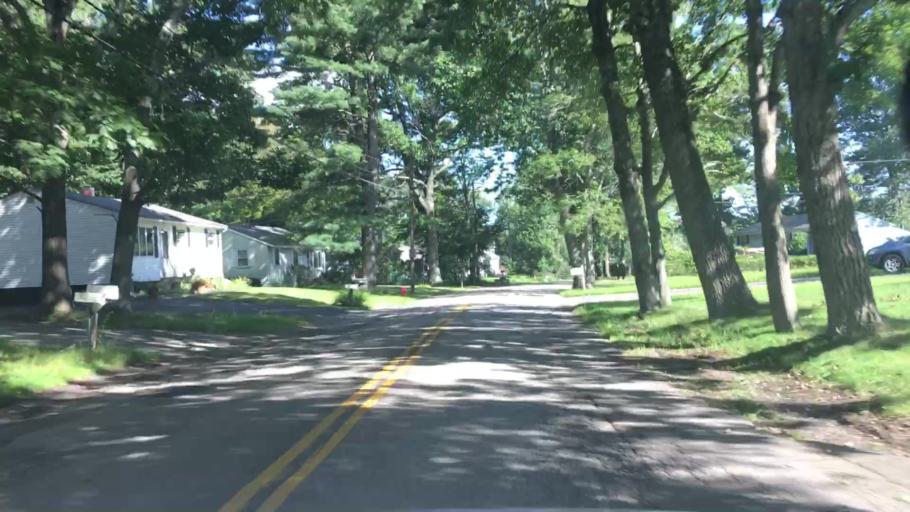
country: US
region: New Hampshire
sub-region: Strafford County
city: Dover
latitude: 43.1577
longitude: -70.8699
